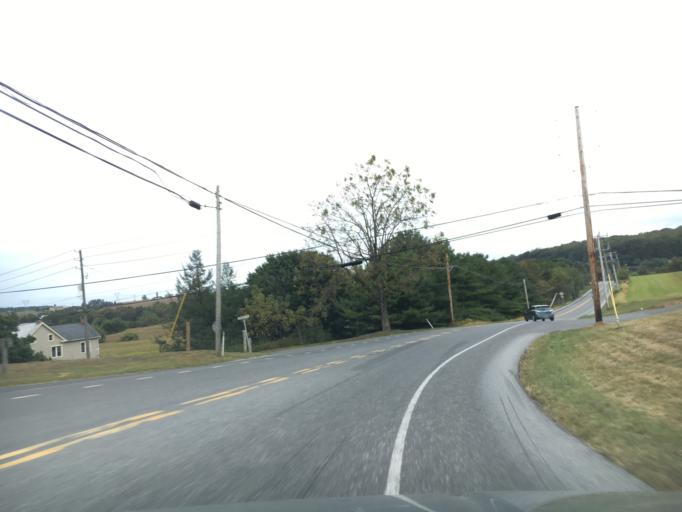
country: US
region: Pennsylvania
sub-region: Lancaster County
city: Quarryville
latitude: 39.8780
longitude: -76.2122
